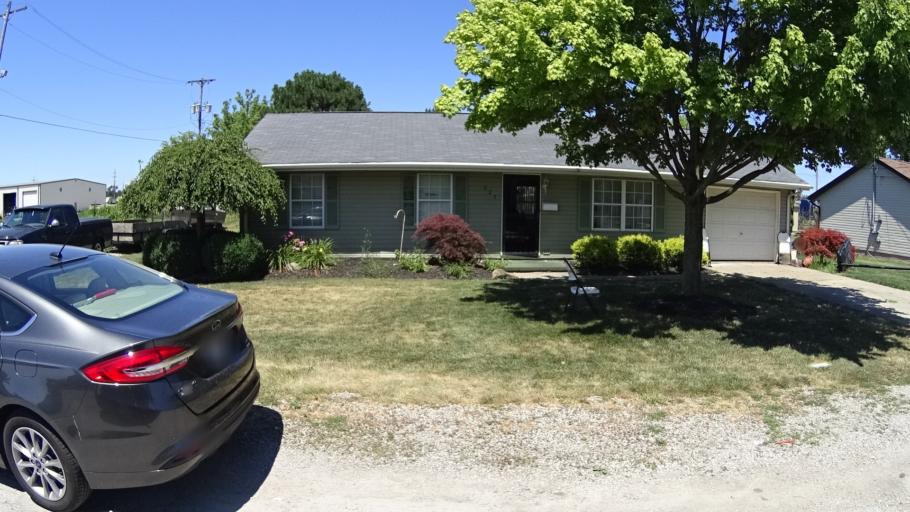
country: US
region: Ohio
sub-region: Erie County
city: Sandusky
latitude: 41.4308
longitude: -82.7011
